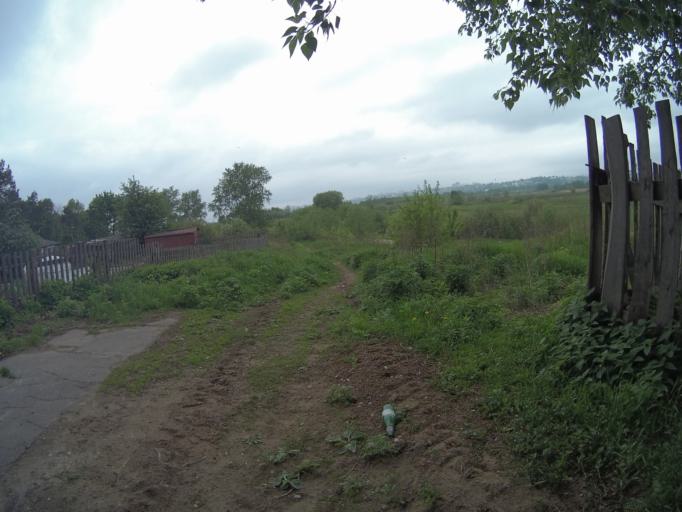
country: RU
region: Vladimir
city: Kommunar
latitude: 56.1120
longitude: 40.4322
